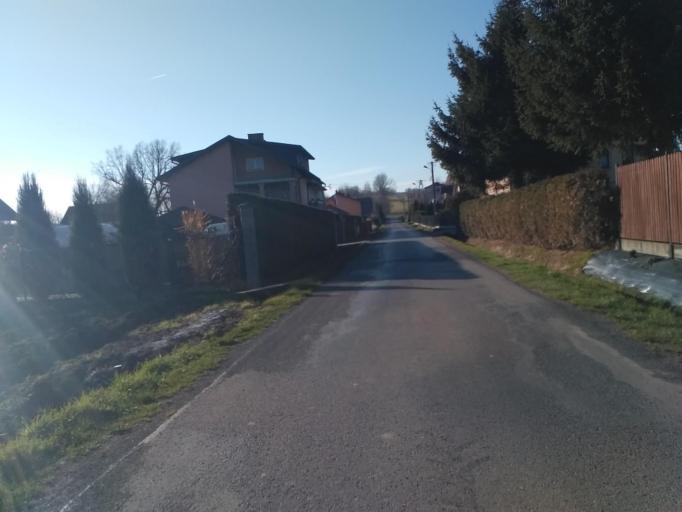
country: PL
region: Subcarpathian Voivodeship
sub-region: Powiat brzozowski
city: Humniska
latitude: 49.6767
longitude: 22.0358
